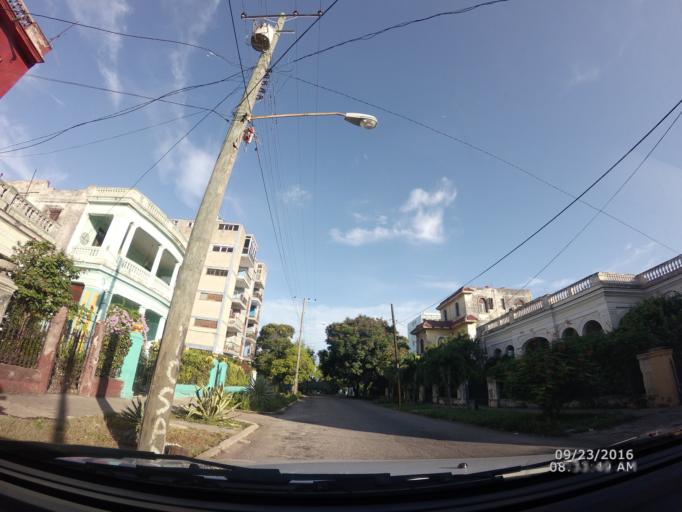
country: CU
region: La Habana
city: Havana
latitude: 23.1298
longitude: -82.3976
